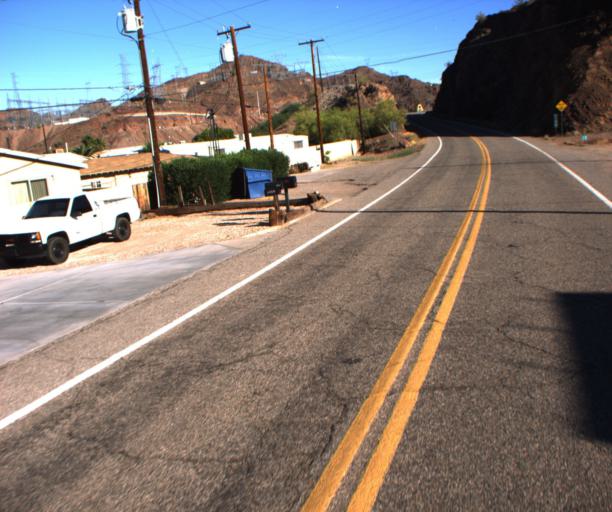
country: US
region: Arizona
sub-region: La Paz County
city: Cienega Springs
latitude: 34.2883
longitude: -114.1360
